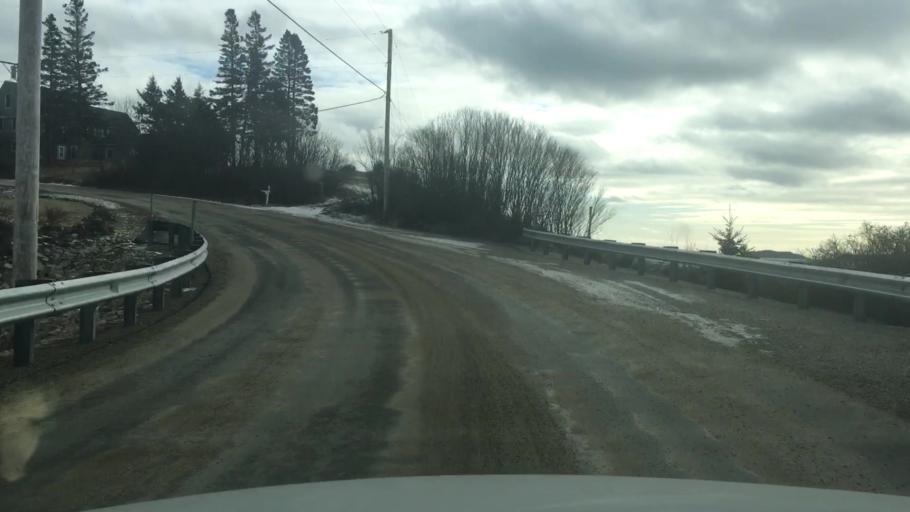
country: US
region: Maine
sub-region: Washington County
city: Machias
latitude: 44.6094
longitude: -67.4765
